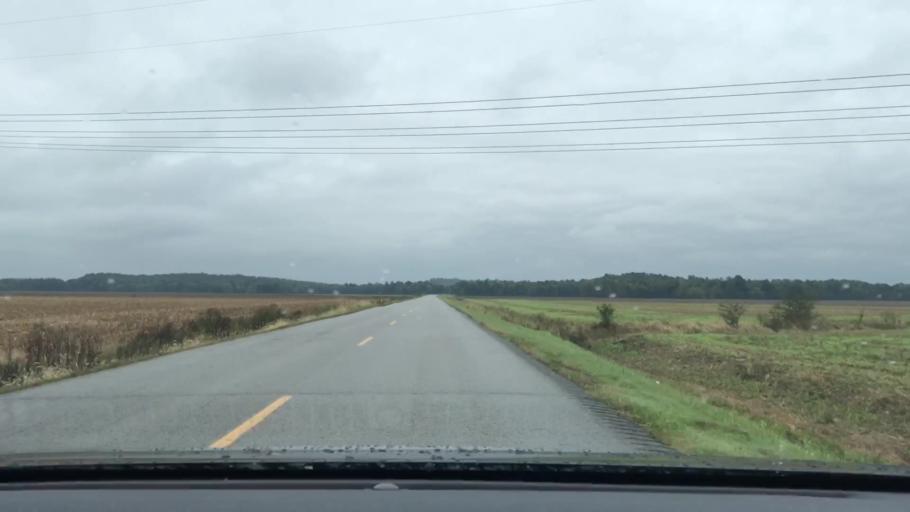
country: US
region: Kentucky
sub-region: McLean County
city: Calhoun
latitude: 37.5037
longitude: -87.2496
